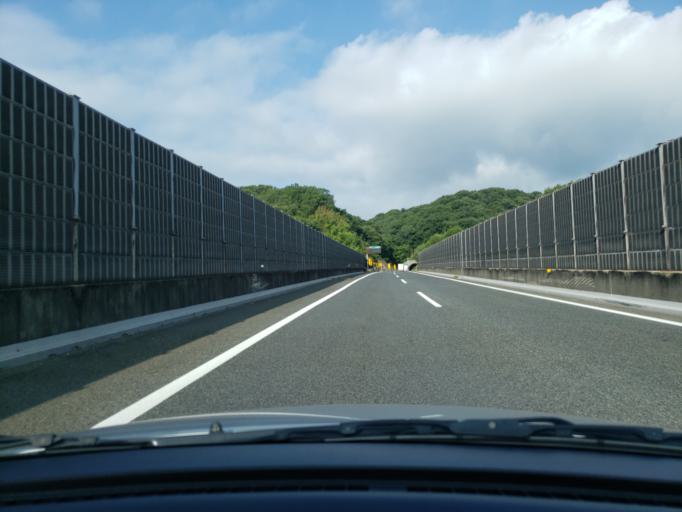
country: JP
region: Hiroshima
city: Fukuyama
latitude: 34.5141
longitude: 133.3609
